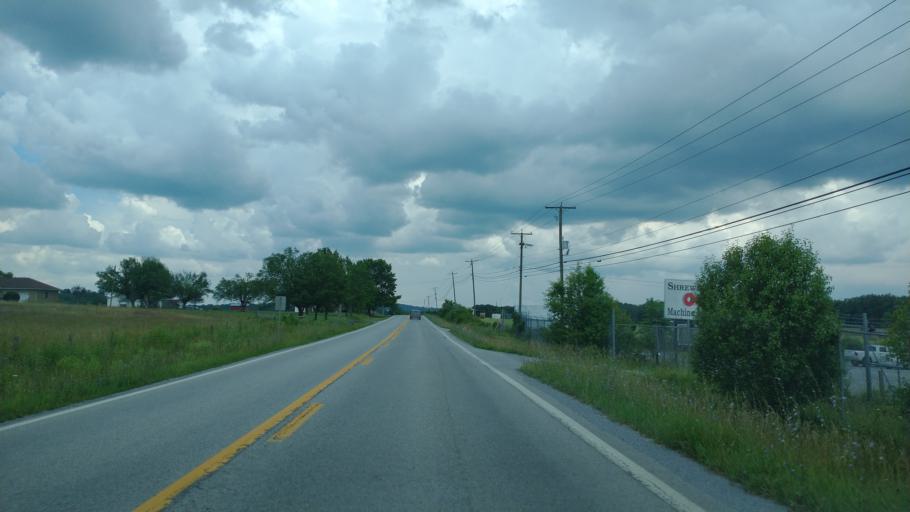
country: US
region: West Virginia
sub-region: Mercer County
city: Athens
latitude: 37.4536
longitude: -81.0088
